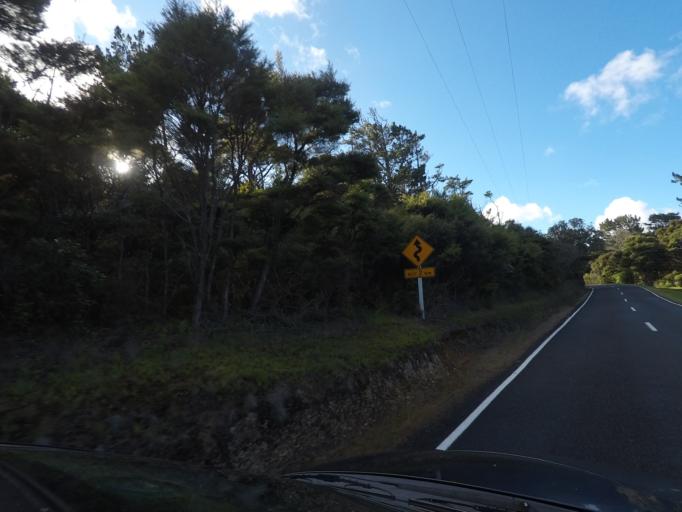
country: NZ
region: Auckland
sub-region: Auckland
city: Titirangi
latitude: -37.0030
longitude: 174.5974
